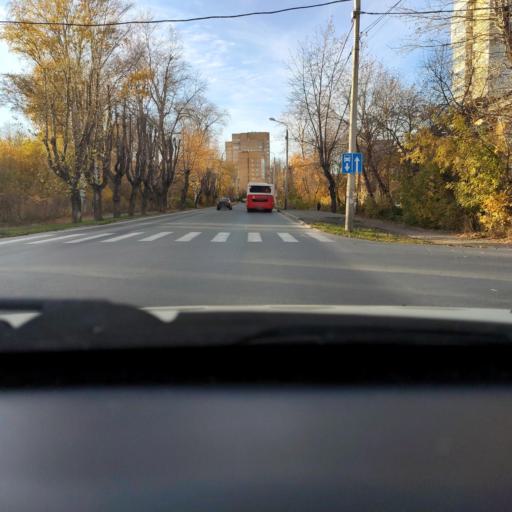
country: RU
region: Perm
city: Perm
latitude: 57.9998
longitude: 56.1834
